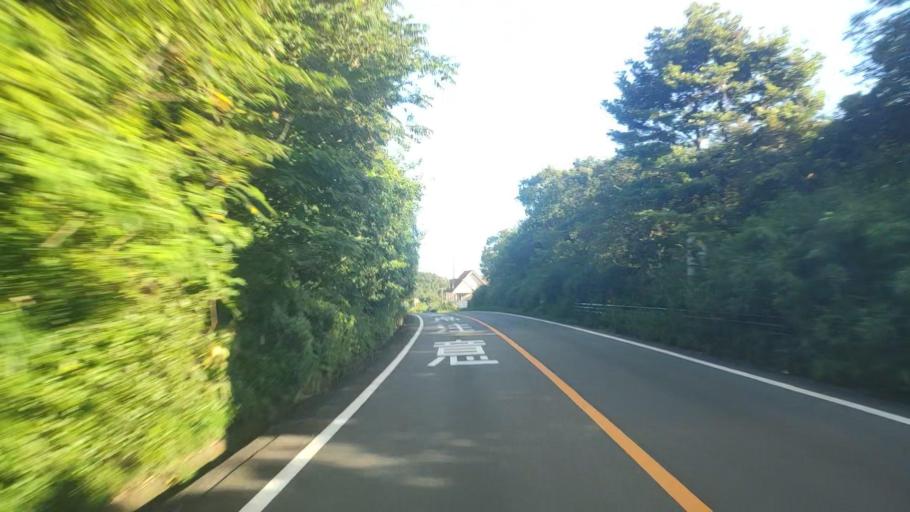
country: JP
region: Mie
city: Toba
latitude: 34.3435
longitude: 136.8396
